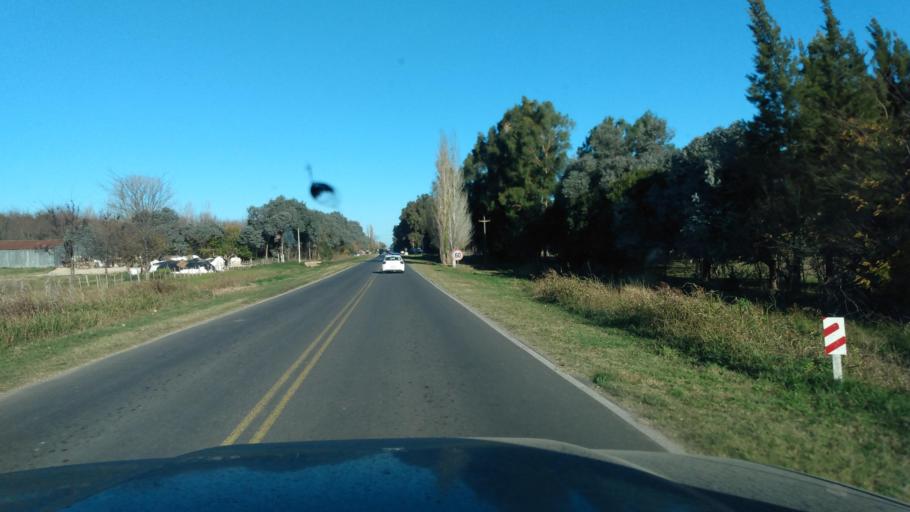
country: AR
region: Buenos Aires
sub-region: Partido de Lujan
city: Lujan
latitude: -34.5268
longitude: -59.1709
